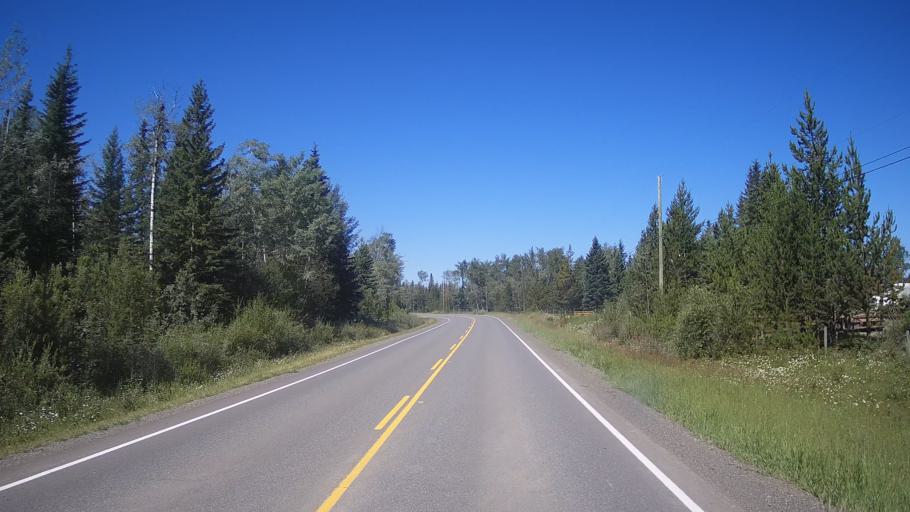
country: CA
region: British Columbia
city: Cache Creek
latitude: 51.5473
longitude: -120.9244
